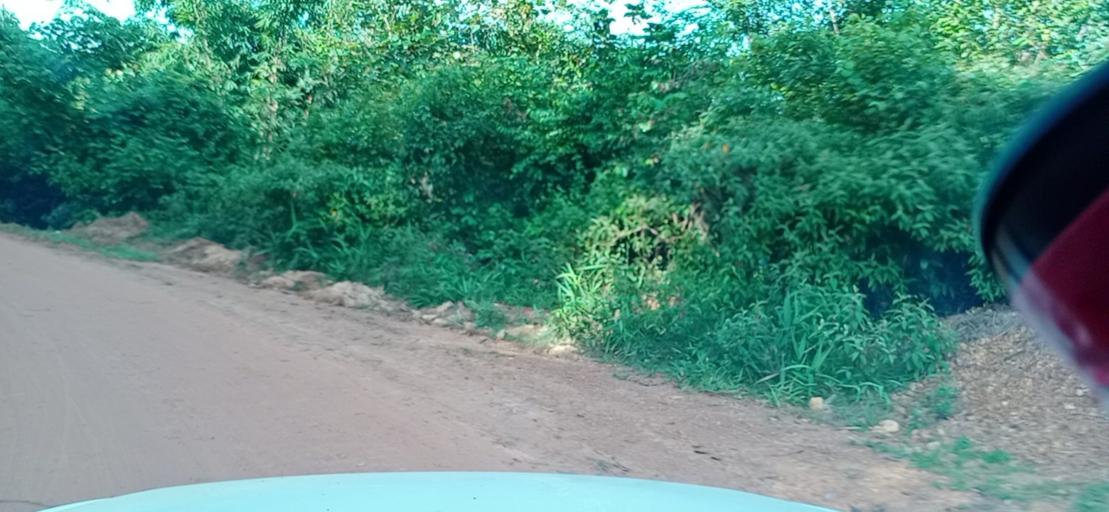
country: TH
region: Changwat Bueng Kan
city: Pak Khat
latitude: 18.6630
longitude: 103.1963
